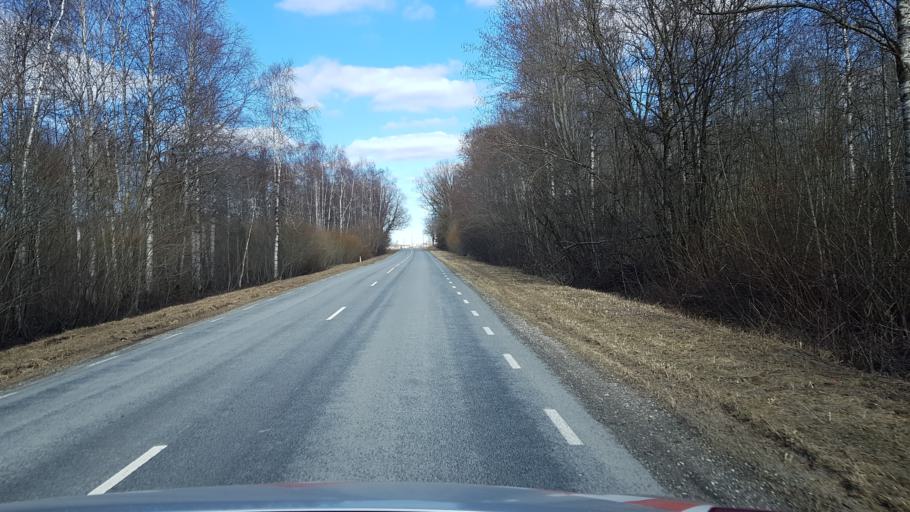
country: EE
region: Laeaene-Virumaa
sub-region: Tapa vald
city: Tapa
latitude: 59.2631
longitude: 25.8475
